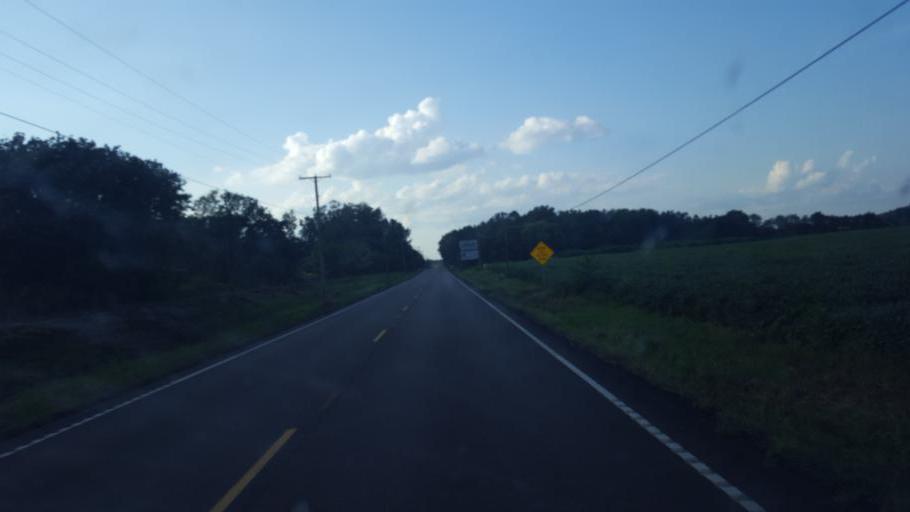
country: US
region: Ohio
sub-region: Knox County
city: Mount Vernon
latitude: 40.4165
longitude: -82.5017
